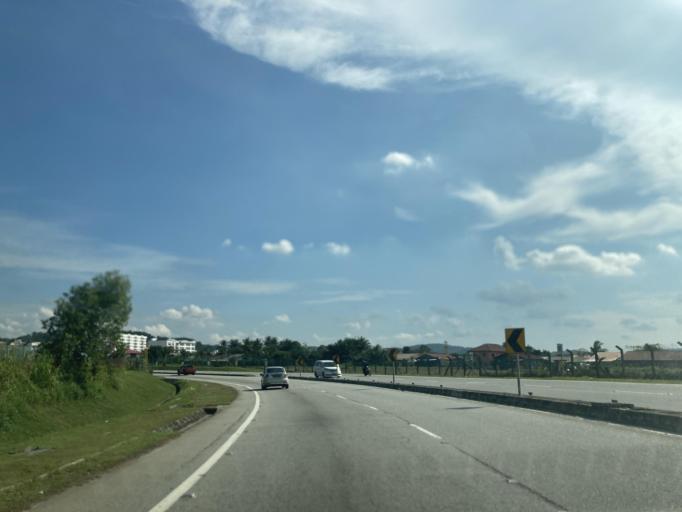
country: MY
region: Selangor
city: Kampung Baru Subang
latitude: 3.1490
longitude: 101.5394
